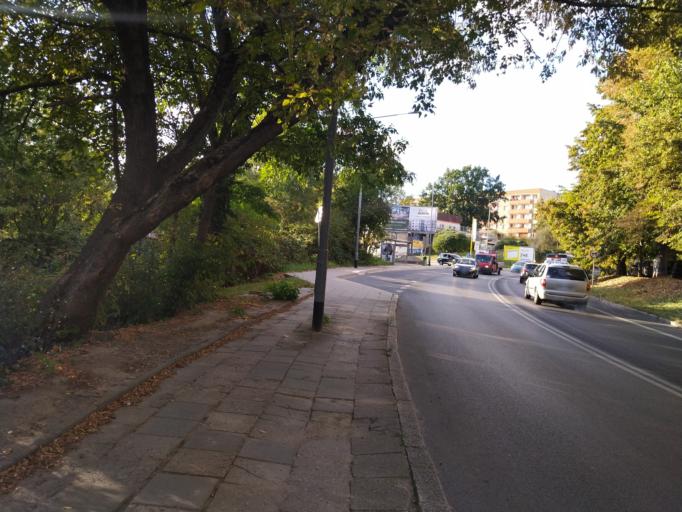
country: PL
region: West Pomeranian Voivodeship
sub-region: Szczecin
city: Szczecin
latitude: 53.4482
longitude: 14.5621
